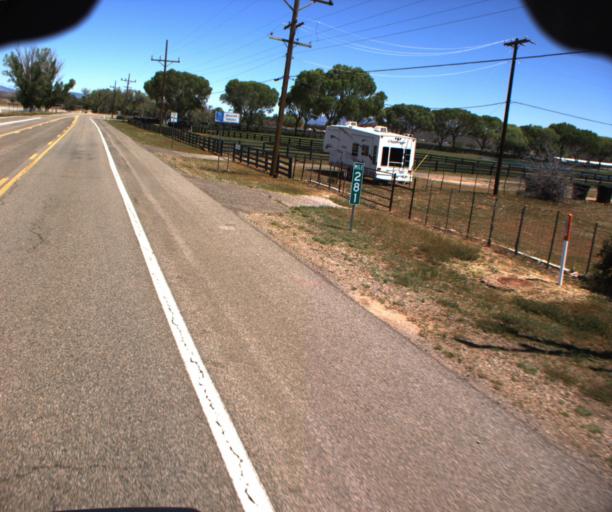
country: US
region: Arizona
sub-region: Yavapai County
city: Congress
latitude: 34.2722
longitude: -112.7272
